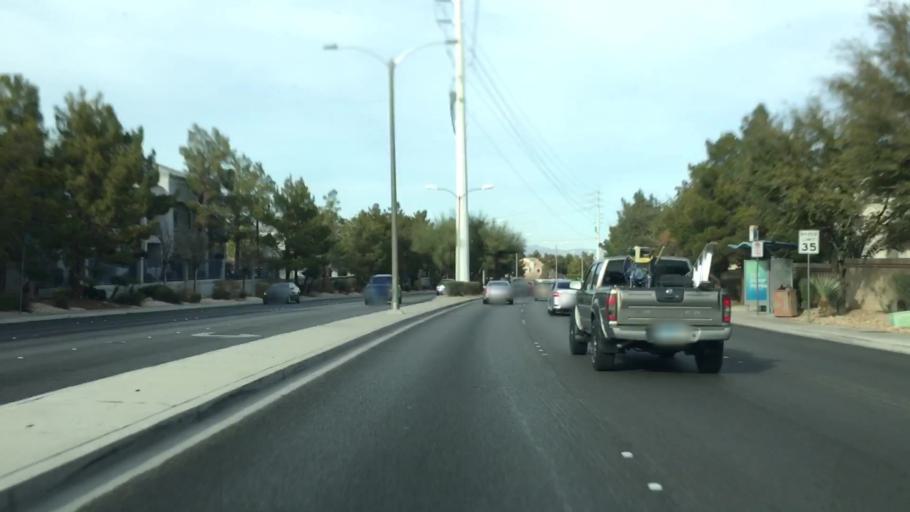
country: US
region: Nevada
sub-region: Clark County
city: Whitney
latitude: 36.0305
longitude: -115.0863
